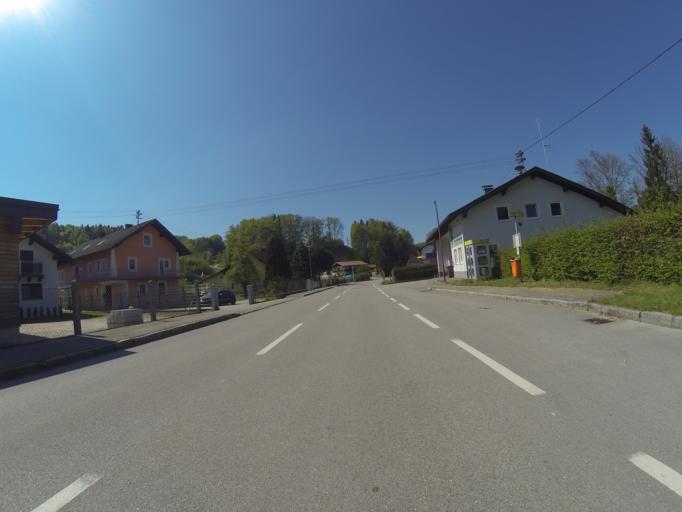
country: AT
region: Upper Austria
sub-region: Politischer Bezirk Gmunden
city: Altmunster
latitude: 47.9475
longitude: 13.7516
